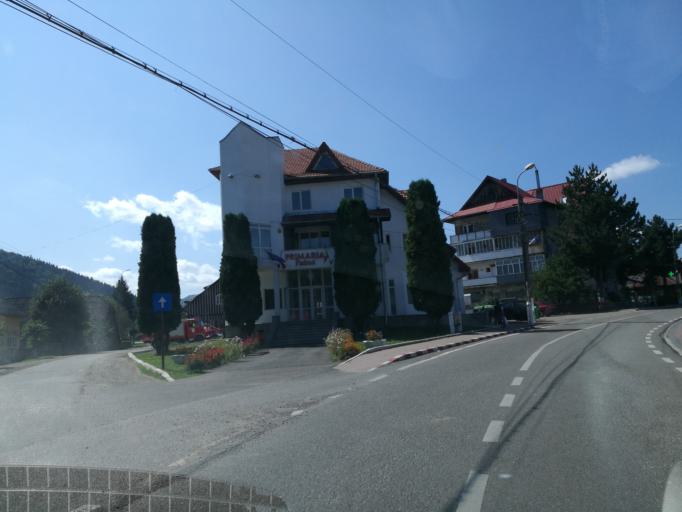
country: RO
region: Suceava
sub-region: Comuna Putna
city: Putna
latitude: 47.8711
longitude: 25.6128
